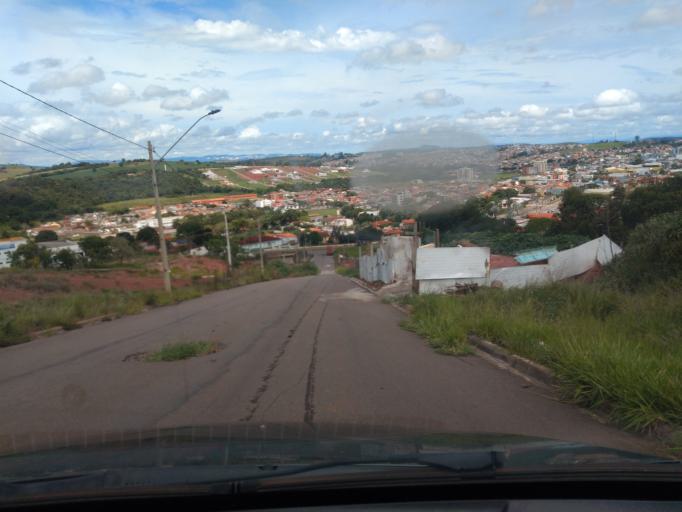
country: BR
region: Minas Gerais
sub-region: Tres Coracoes
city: Tres Coracoes
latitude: -21.6707
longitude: -45.2752
